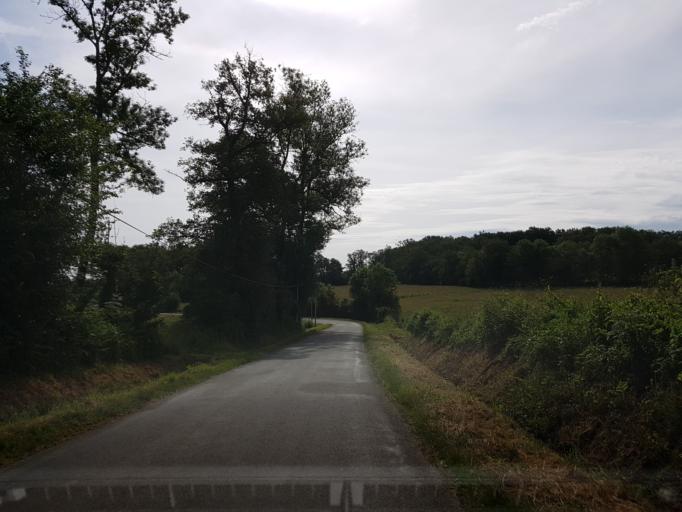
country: FR
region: Poitou-Charentes
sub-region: Departement de la Charente
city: Etagnac
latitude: 45.9380
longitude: 0.7516
